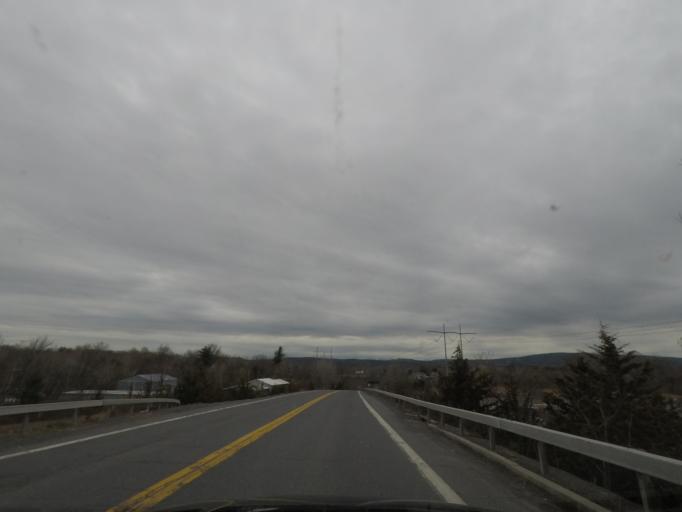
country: US
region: New York
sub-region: Rensselaer County
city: Castleton-on-Hudson
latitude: 42.5419
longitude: -73.8175
